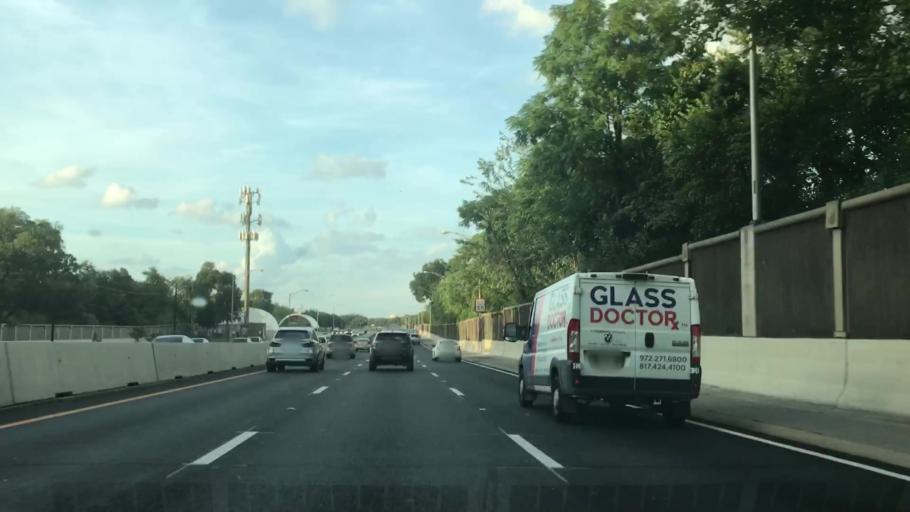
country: US
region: Texas
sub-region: Dallas County
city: University Park
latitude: 32.8823
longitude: -96.8093
